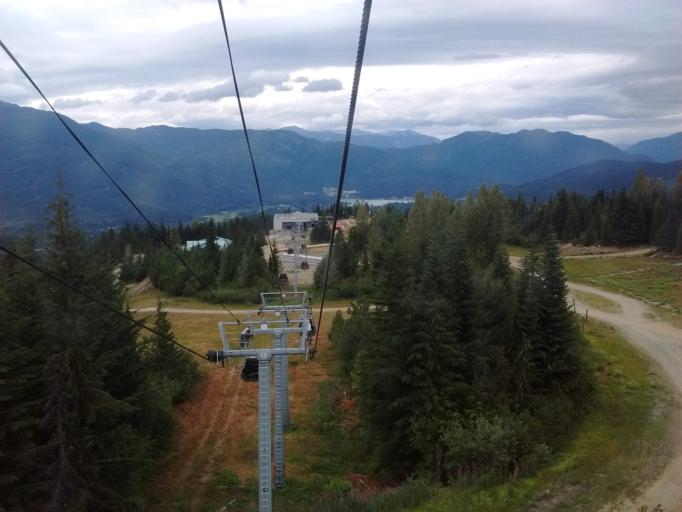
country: CA
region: British Columbia
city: Whistler
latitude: 50.0955
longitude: -122.9508
